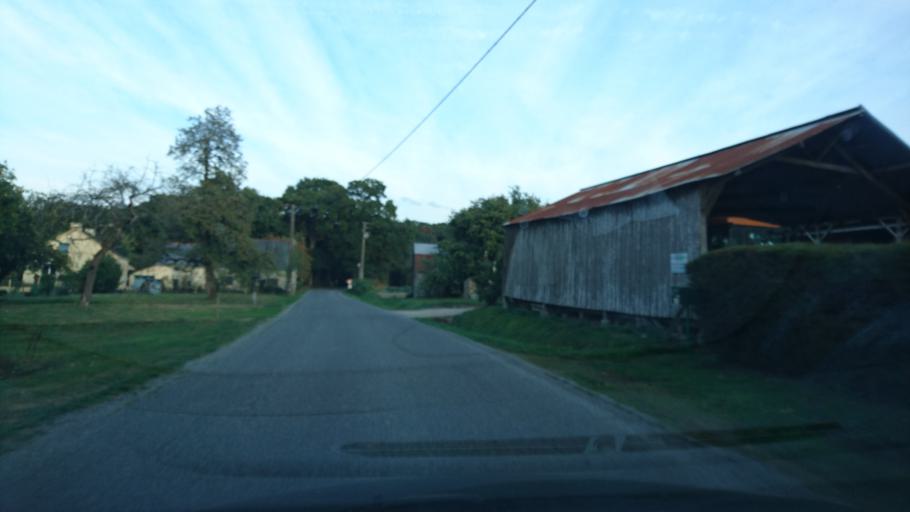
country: FR
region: Brittany
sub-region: Departement d'Ille-et-Vilaine
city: Bains-sur-Oust
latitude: 47.7063
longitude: -2.0576
